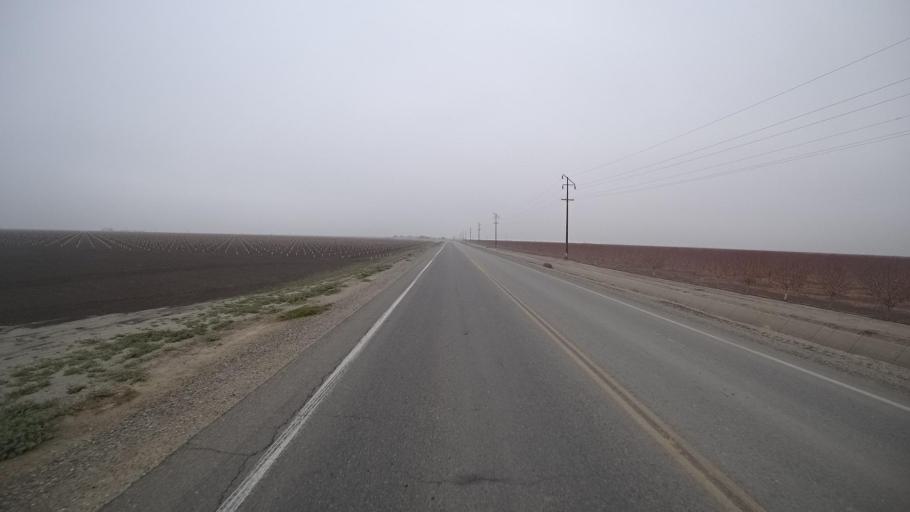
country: US
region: California
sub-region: Kern County
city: Greenfield
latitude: 35.1523
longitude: -119.1098
